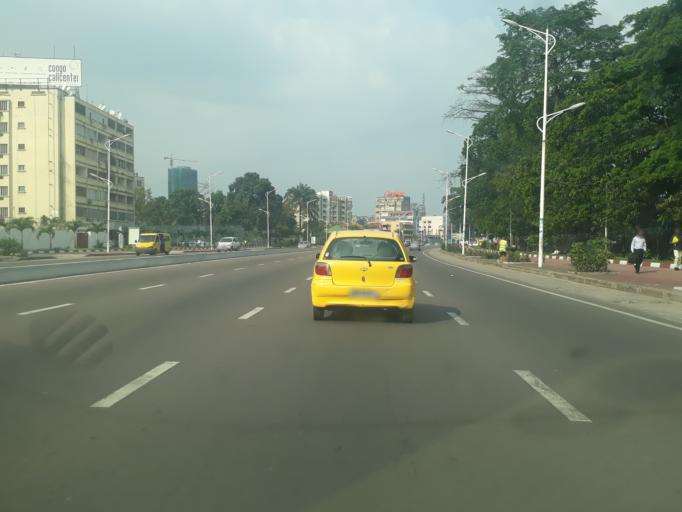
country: CD
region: Kinshasa
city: Kinshasa
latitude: -4.3082
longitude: 15.2929
